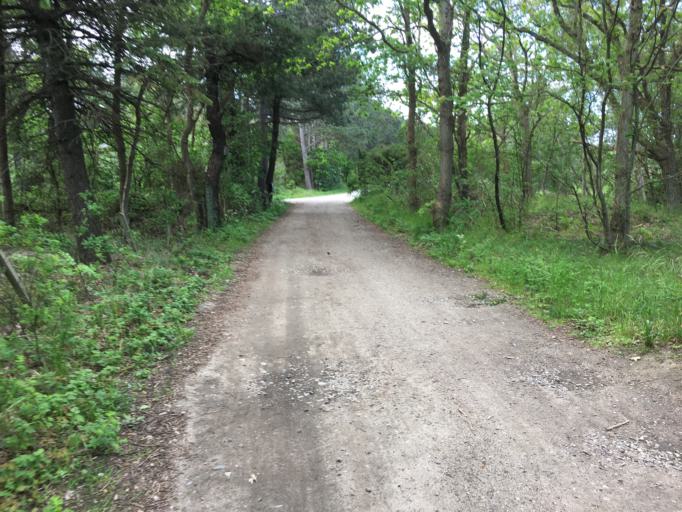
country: DK
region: Zealand
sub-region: Odsherred Kommune
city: Nykobing Sjaelland
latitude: 55.9654
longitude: 11.7493
